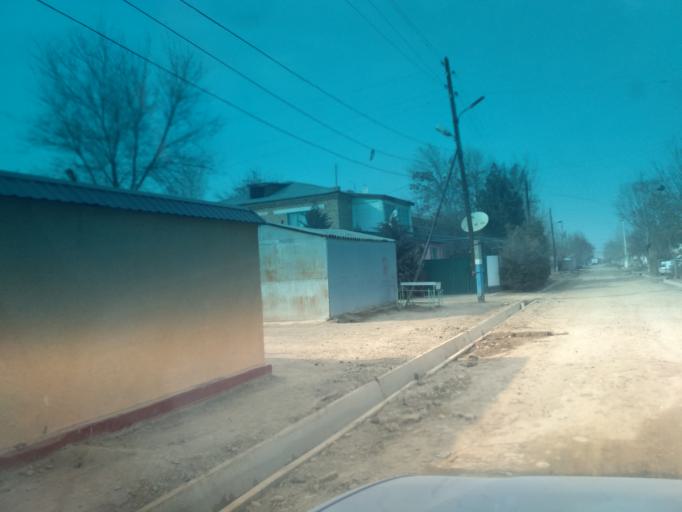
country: UZ
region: Sirdaryo
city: Guliston
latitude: 40.5008
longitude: 68.7807
